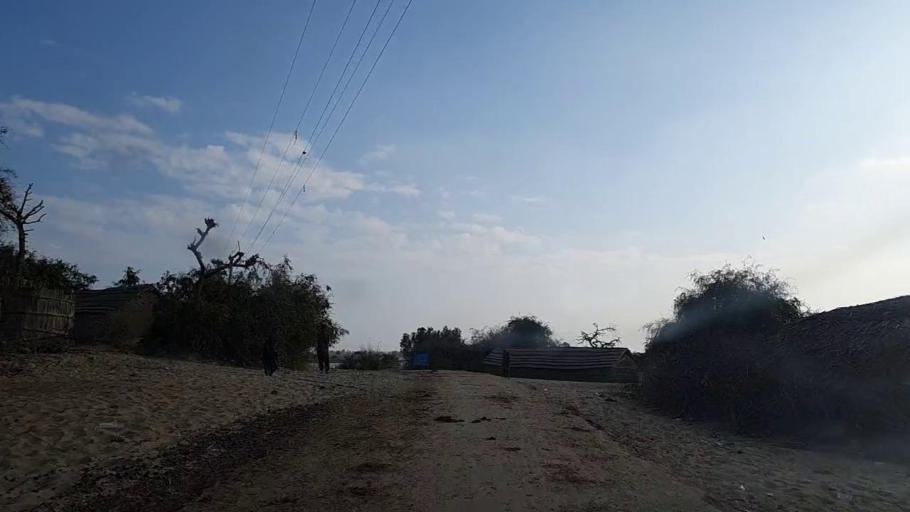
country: PK
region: Sindh
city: Sanghar
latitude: 26.2018
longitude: 69.0277
